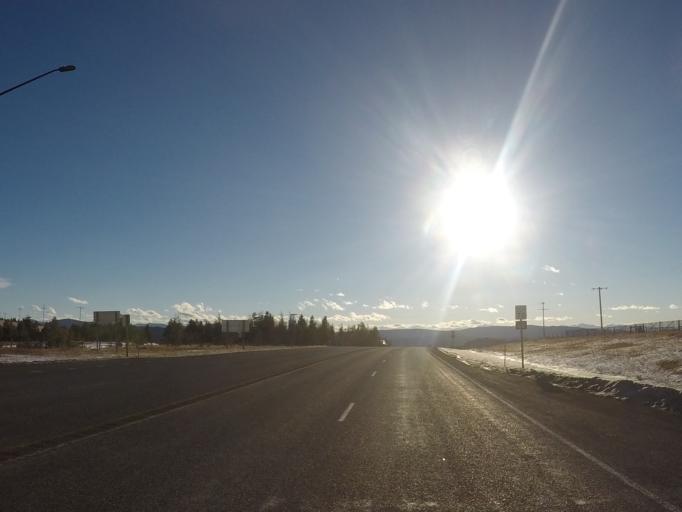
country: US
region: Montana
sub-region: Lewis and Clark County
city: Helena West Side
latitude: 46.5616
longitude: -112.3092
